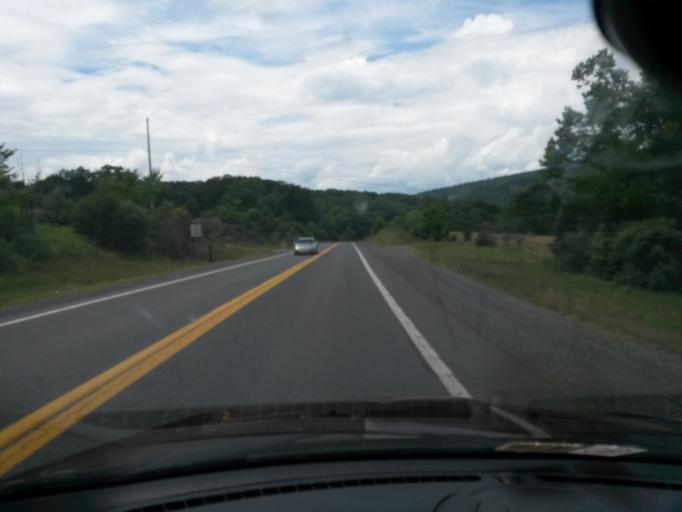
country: US
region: West Virginia
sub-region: Grant County
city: Petersburg
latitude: 38.9968
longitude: -79.0650
